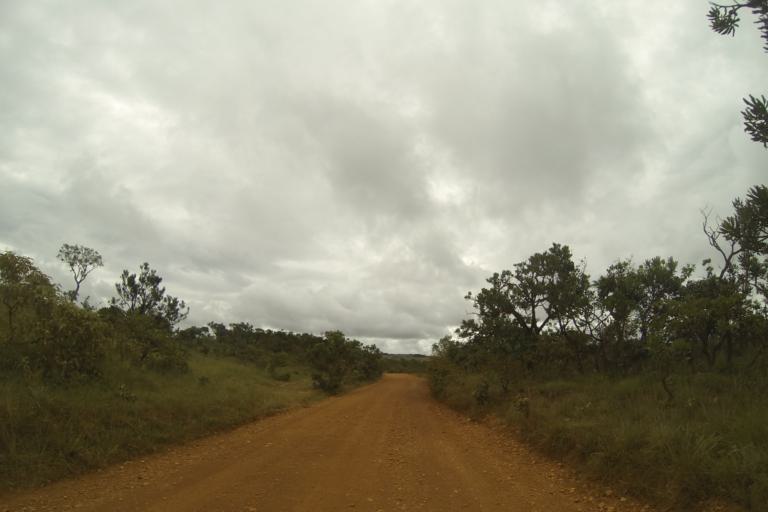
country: BR
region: Minas Gerais
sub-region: Ibia
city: Ibia
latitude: -19.7429
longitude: -46.4646
